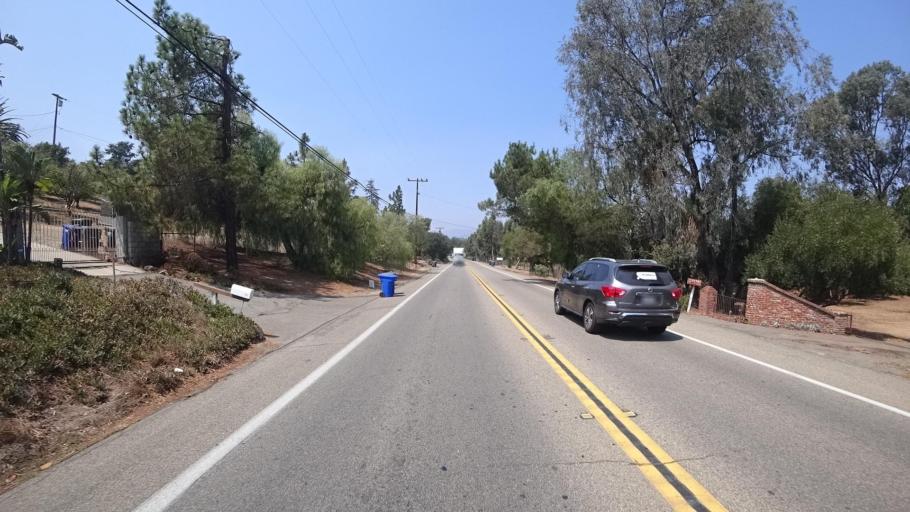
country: US
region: California
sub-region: San Diego County
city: Fallbrook
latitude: 33.3892
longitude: -117.2215
